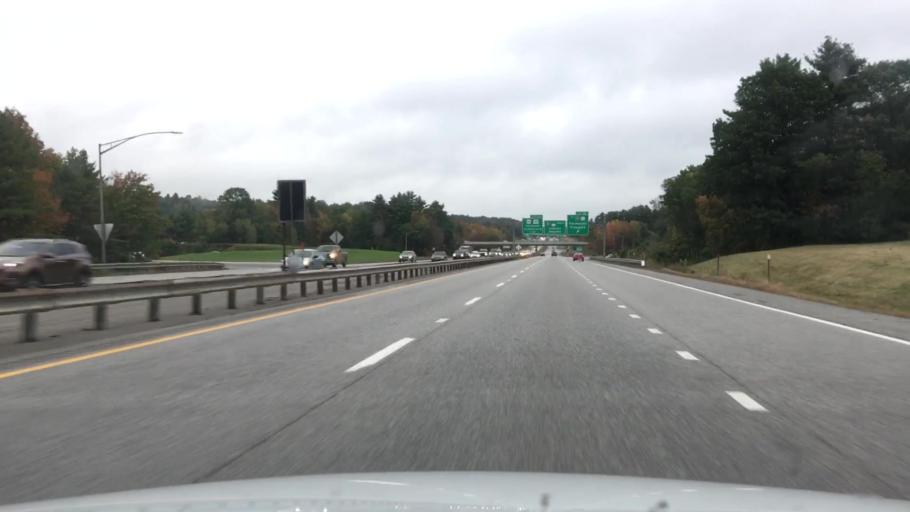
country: US
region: Maine
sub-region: Cumberland County
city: Falmouth
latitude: 43.7173
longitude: -70.3058
